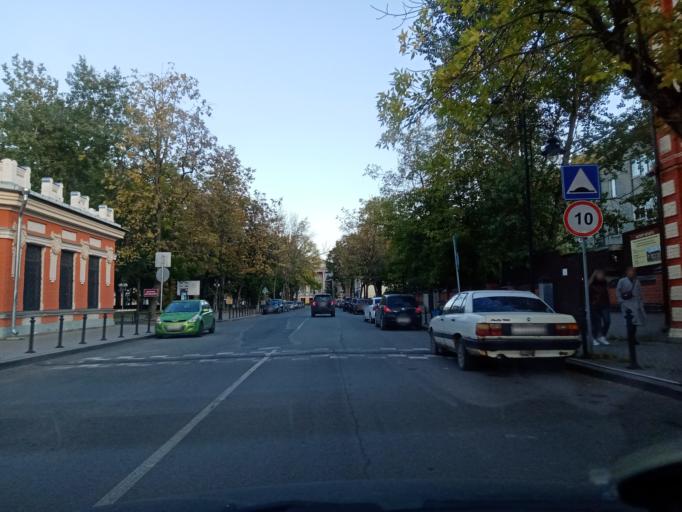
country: RU
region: Pskov
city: Pskov
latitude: 57.8169
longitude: 28.3389
